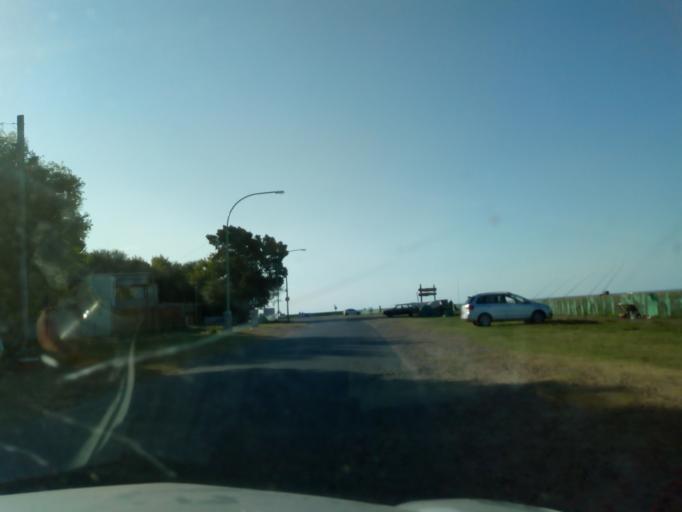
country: AR
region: Buenos Aires
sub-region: Partido de Ensenada
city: Ensenada
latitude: -34.7923
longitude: -57.9960
